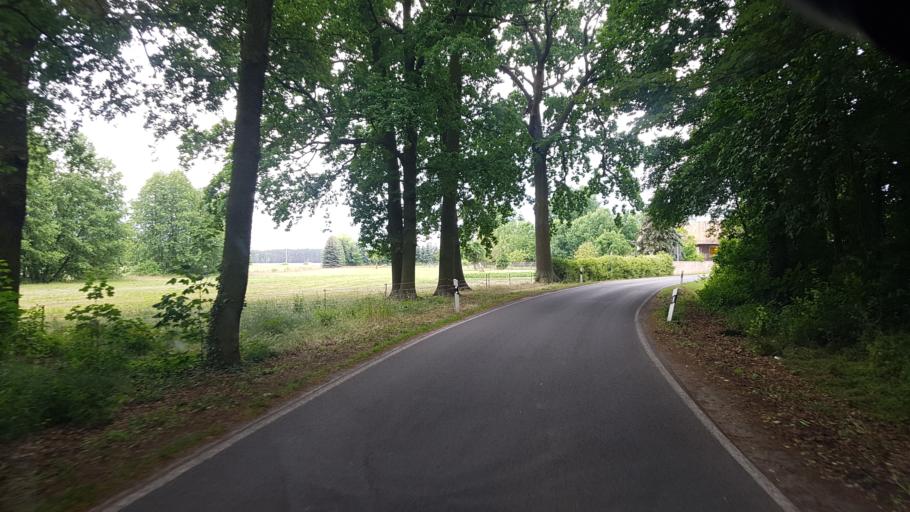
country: DE
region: Saxony-Anhalt
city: Holzdorf
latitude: 51.8017
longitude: 13.2368
